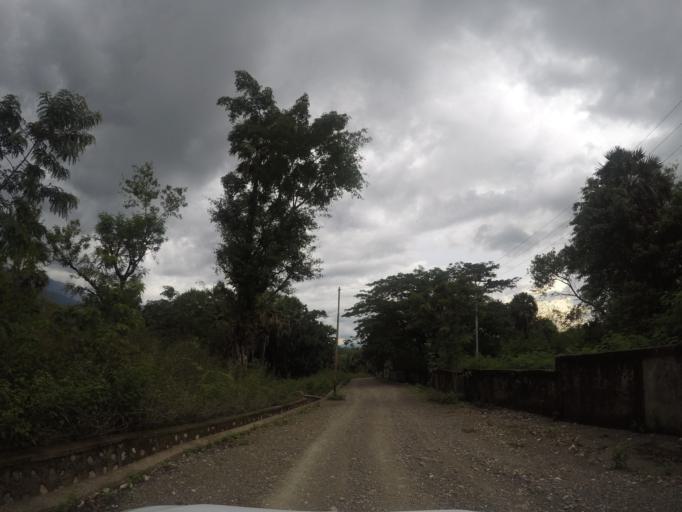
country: TL
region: Bobonaro
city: Maliana
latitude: -8.9744
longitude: 125.2258
